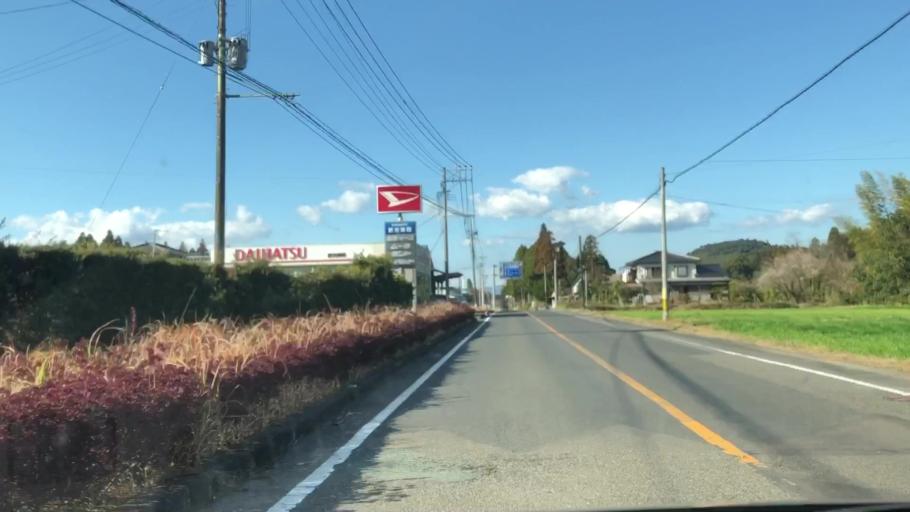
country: JP
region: Kagoshima
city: Satsumasendai
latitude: 31.7976
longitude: 130.4404
